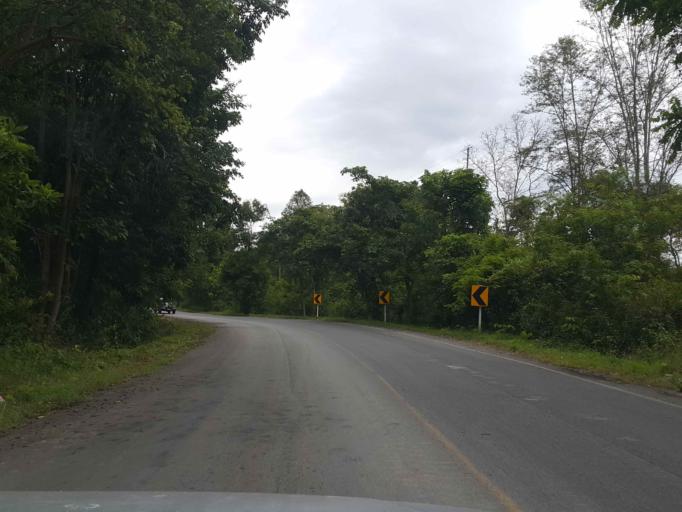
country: TH
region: Lampang
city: Thoen
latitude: 17.6112
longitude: 99.3254
